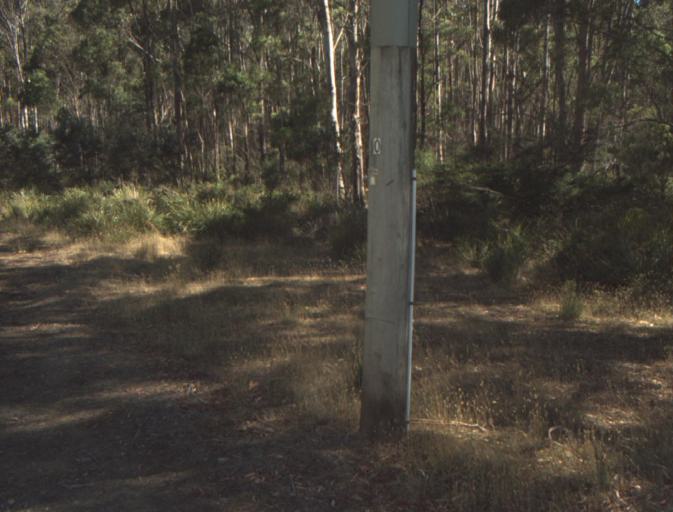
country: AU
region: Tasmania
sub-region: Launceston
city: Newstead
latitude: -41.3048
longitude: 147.3167
